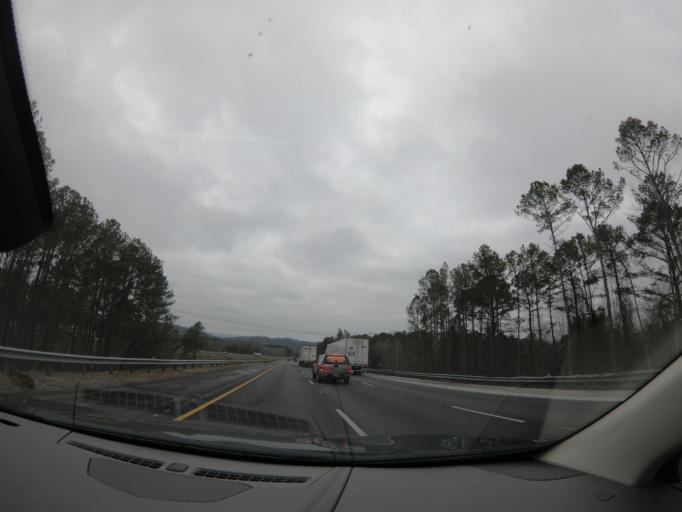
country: US
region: Georgia
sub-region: Catoosa County
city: Indian Springs
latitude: 34.9407
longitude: -85.1658
